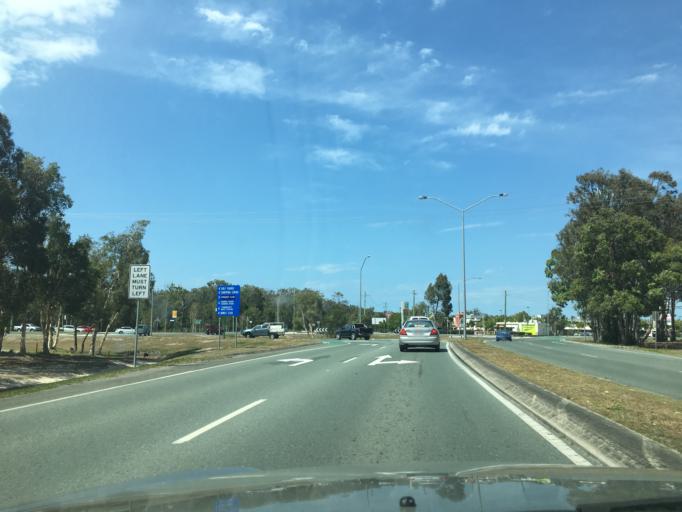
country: AU
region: Queensland
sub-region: Moreton Bay
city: Bongaree
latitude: -27.0647
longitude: 153.1540
